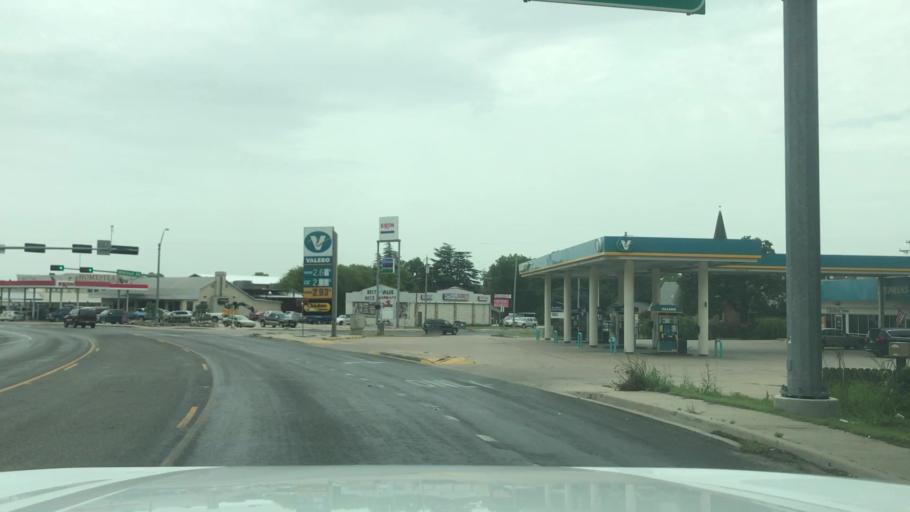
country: US
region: Texas
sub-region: Hamilton County
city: Hico
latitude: 31.9834
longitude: -98.0344
